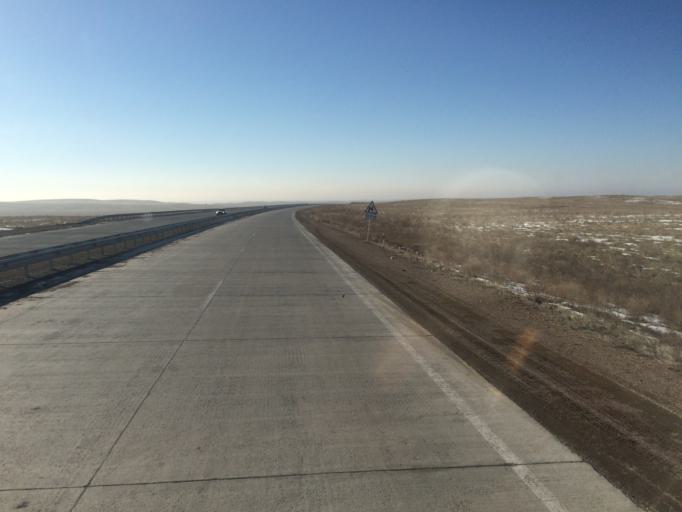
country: KZ
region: Zhambyl
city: Georgiyevka
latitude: 43.3419
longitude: 74.4890
